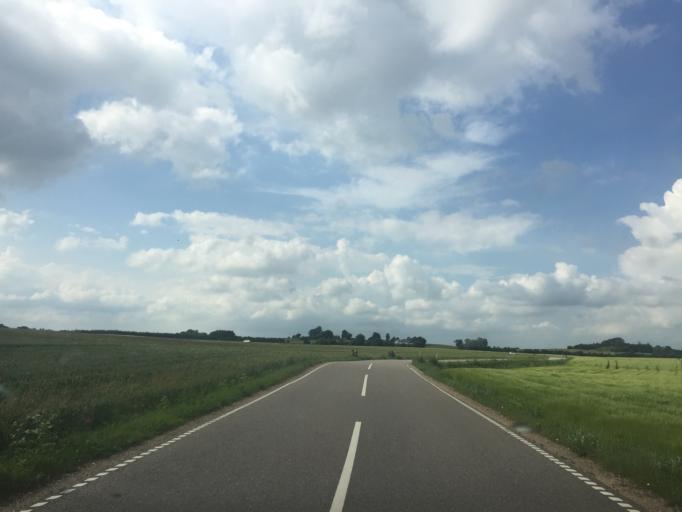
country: DK
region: Capital Region
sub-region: Hoje-Taastrup Kommune
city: Flong
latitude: 55.6844
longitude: 12.1890
